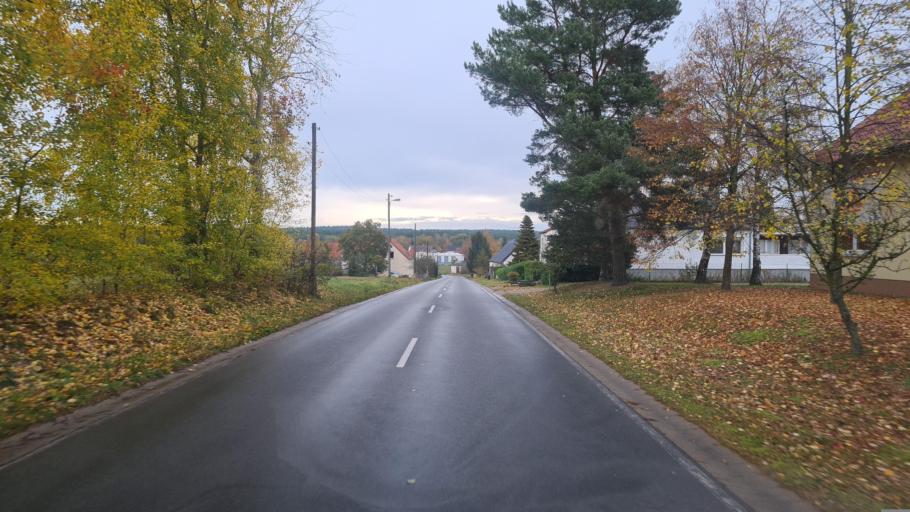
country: DE
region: Saxony-Anhalt
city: Abtsdorf
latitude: 51.9257
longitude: 12.6734
